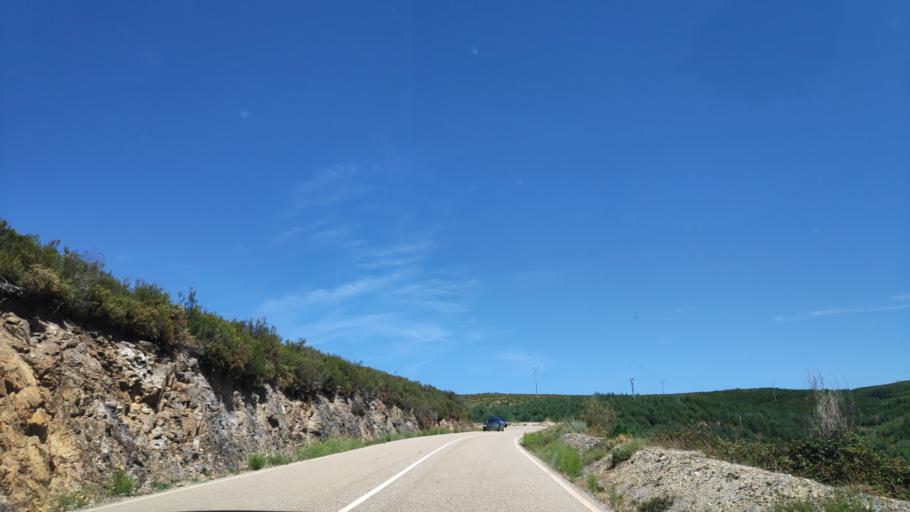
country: ES
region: Castille and Leon
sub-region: Provincia de Zamora
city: Requejo
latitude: 42.0046
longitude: -6.6953
